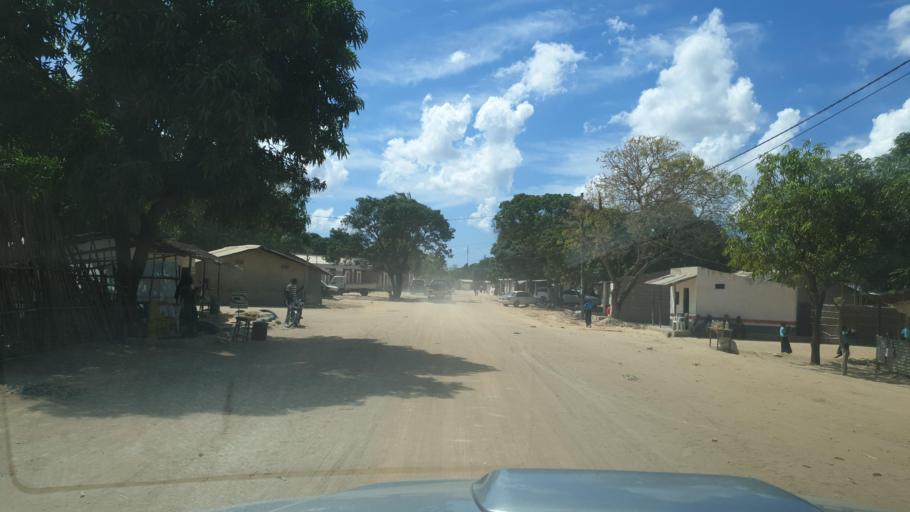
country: MZ
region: Nampula
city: Nacala
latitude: -14.5682
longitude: 40.6963
